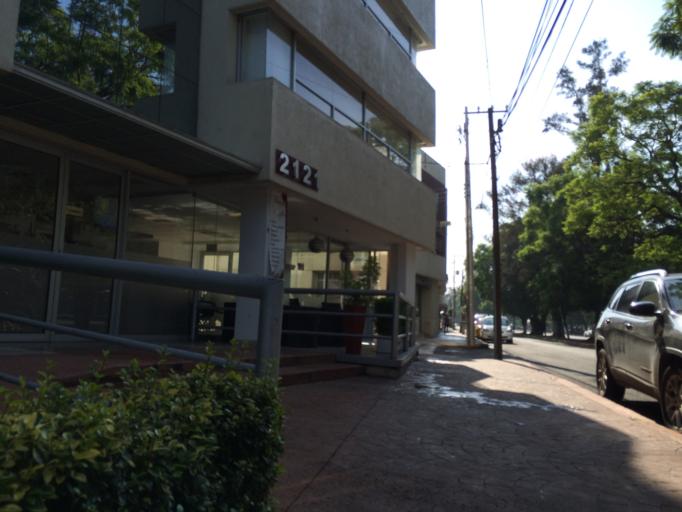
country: MX
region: Michoacan
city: Morelia
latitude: 19.6820
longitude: -101.1731
